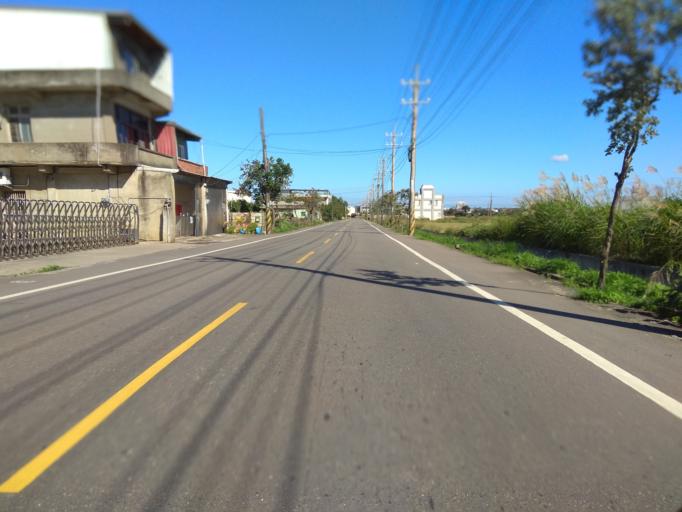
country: TW
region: Taiwan
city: Taoyuan City
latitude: 24.9978
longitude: 121.1364
